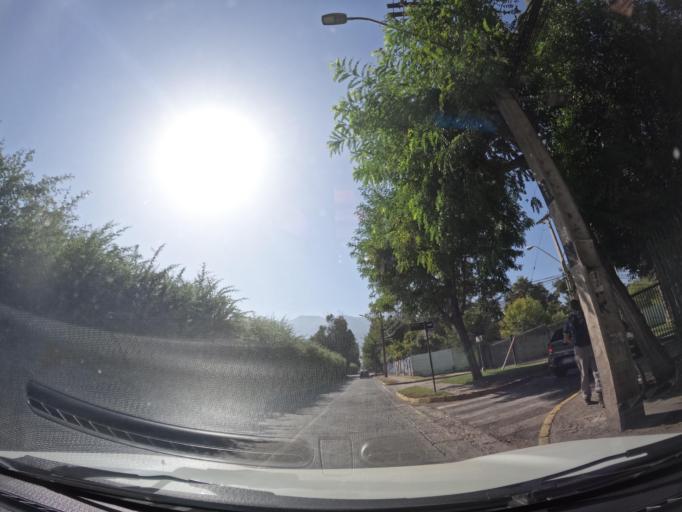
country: CL
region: Santiago Metropolitan
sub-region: Provincia de Santiago
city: Villa Presidente Frei, Nunoa, Santiago, Chile
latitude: -33.5072
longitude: -70.5563
